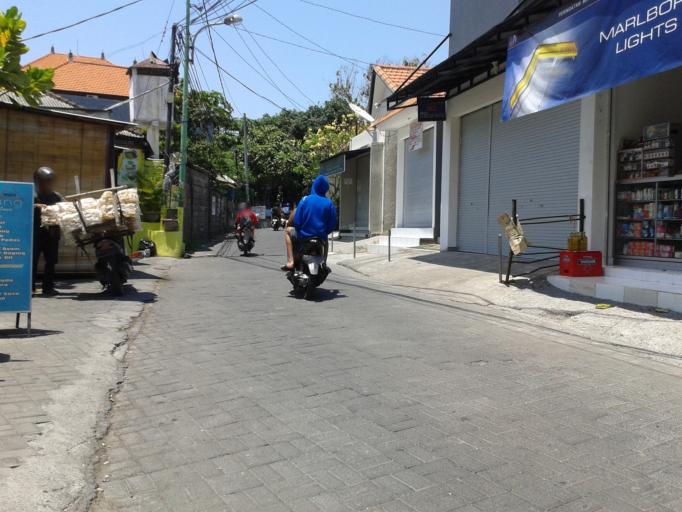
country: ID
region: Bali
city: Kuta
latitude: -8.7059
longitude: 115.1725
